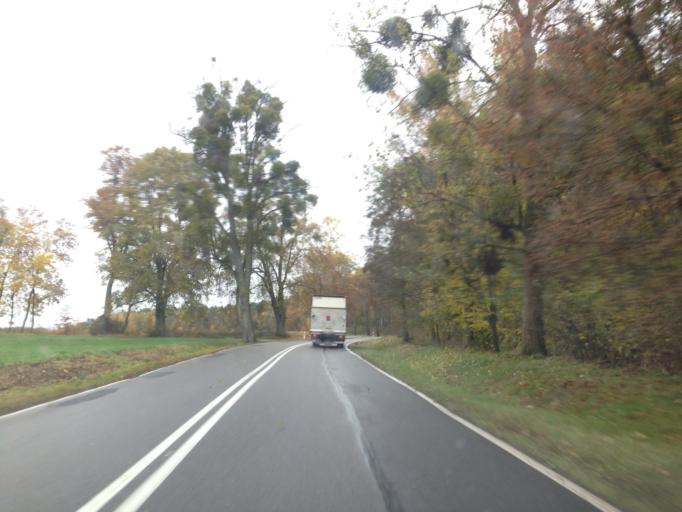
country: PL
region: Pomeranian Voivodeship
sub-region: Powiat kwidzynski
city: Ryjewo
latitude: 53.8491
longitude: 18.9991
